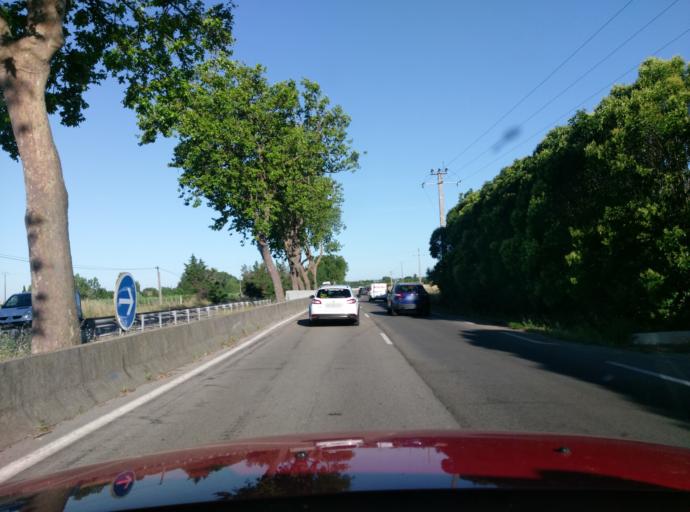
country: FR
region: Languedoc-Roussillon
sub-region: Departement du Gard
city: Rodilhan
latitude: 43.8307
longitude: 4.4508
